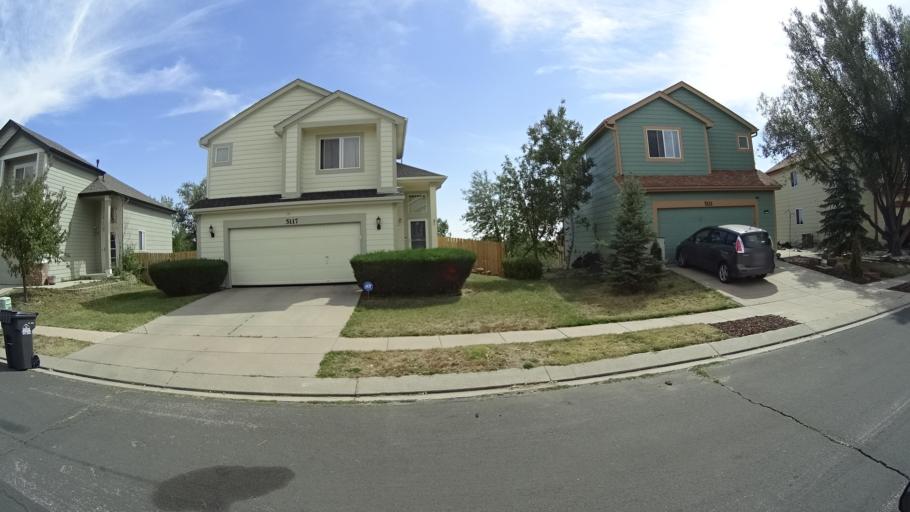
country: US
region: Colorado
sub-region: El Paso County
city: Cimarron Hills
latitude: 38.9041
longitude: -104.7089
